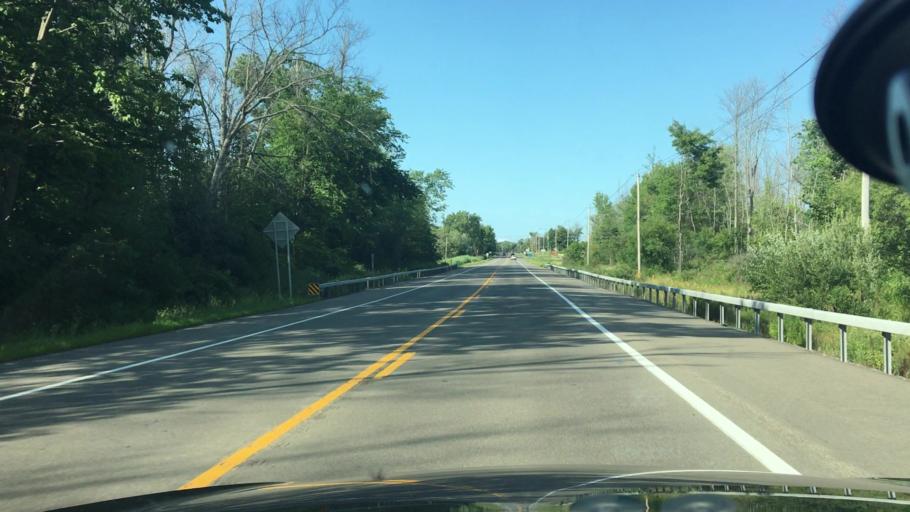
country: US
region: New York
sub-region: Erie County
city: Eden
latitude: 42.6824
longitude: -78.9463
